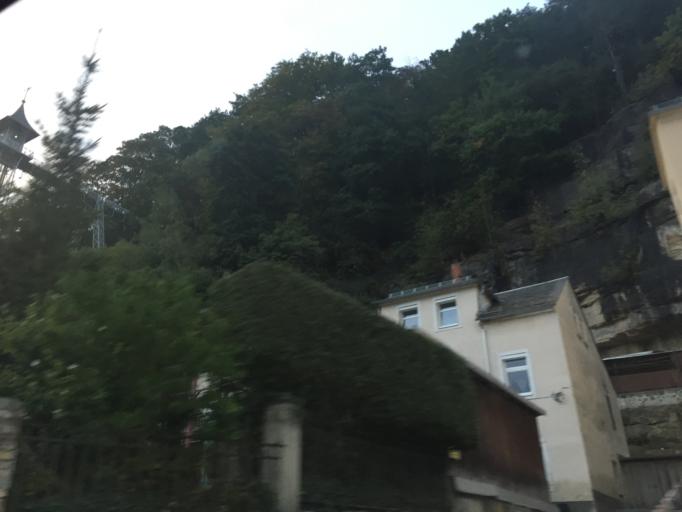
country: DE
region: Saxony
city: Bad Schandau
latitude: 50.9162
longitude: 14.1622
